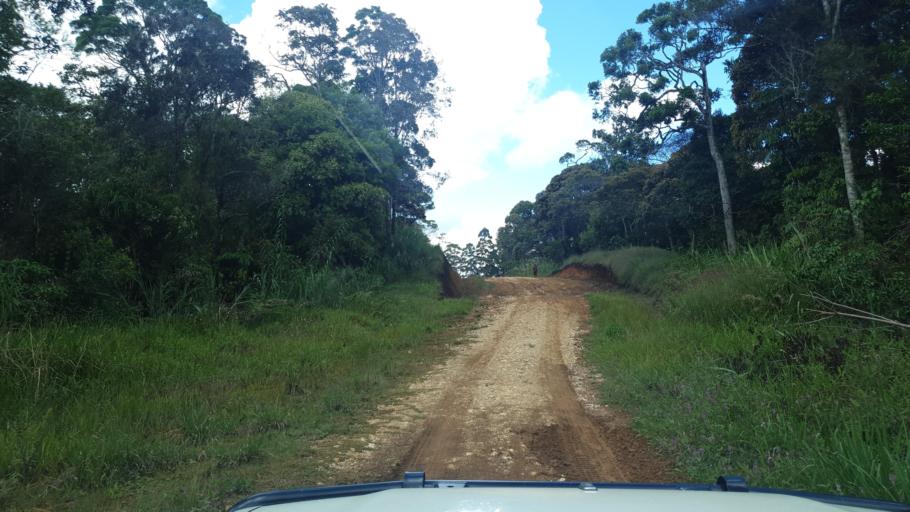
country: PG
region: Eastern Highlands
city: Goroka
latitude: -6.2791
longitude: 145.1959
